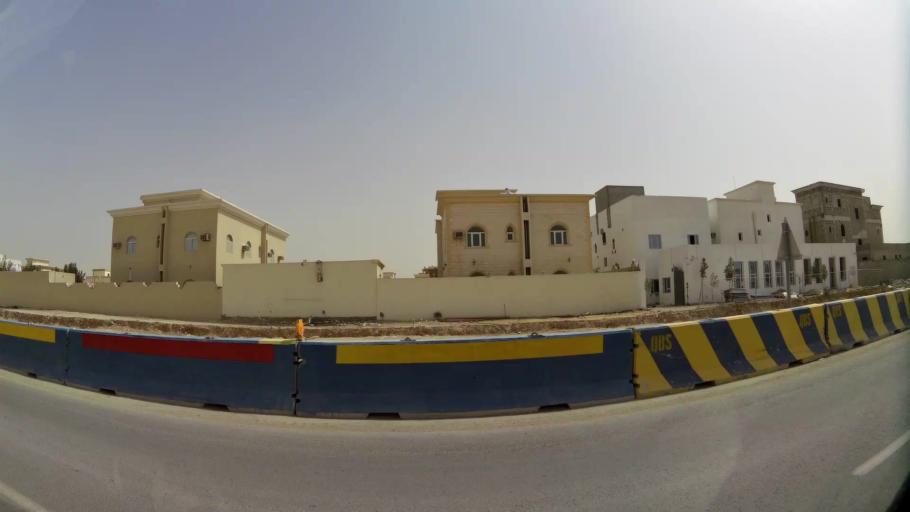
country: QA
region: Baladiyat ar Rayyan
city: Ar Rayyan
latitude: 25.2519
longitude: 51.3634
